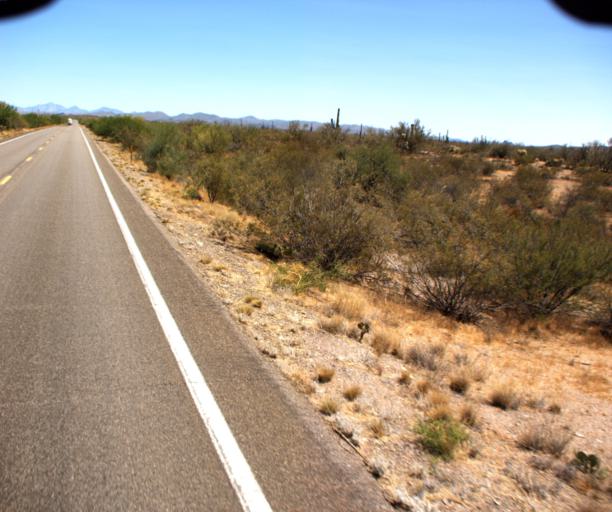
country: US
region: Arizona
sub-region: Pima County
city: Catalina
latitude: 32.7178
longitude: -111.1054
